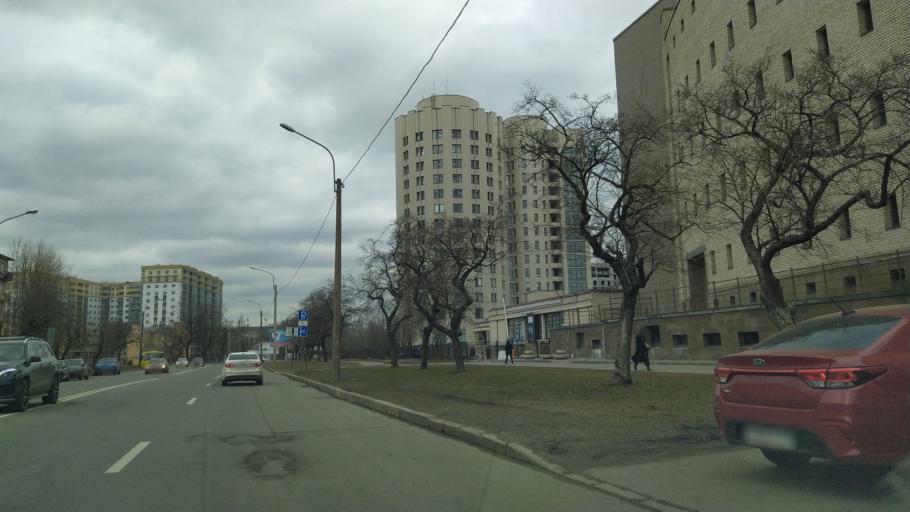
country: RU
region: St.-Petersburg
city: Centralniy
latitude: 59.9313
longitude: 30.4165
